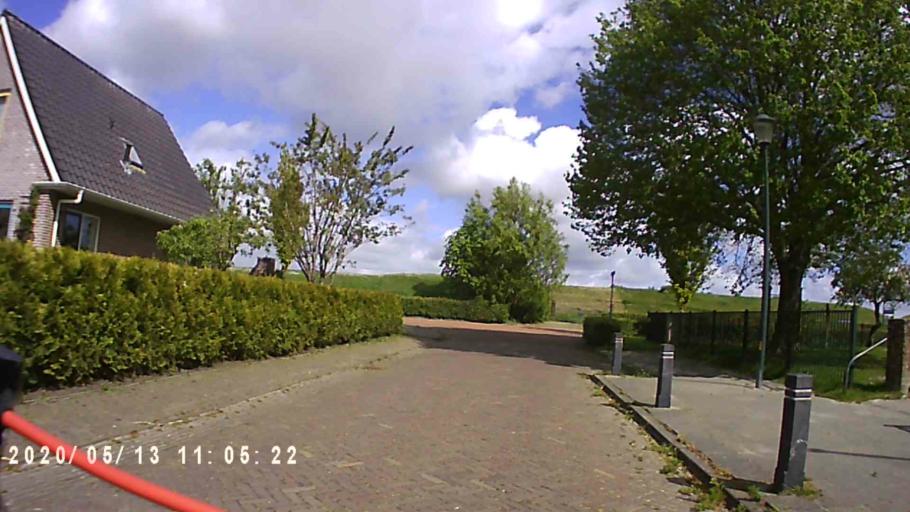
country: NL
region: Groningen
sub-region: Gemeente Zuidhorn
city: Grijpskerk
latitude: 53.2876
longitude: 6.3274
